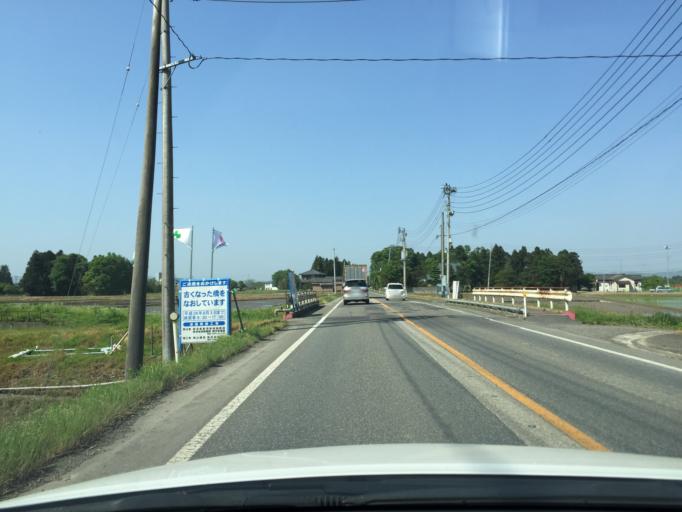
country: JP
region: Niigata
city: Muramatsu
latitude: 37.7161
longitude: 139.2173
